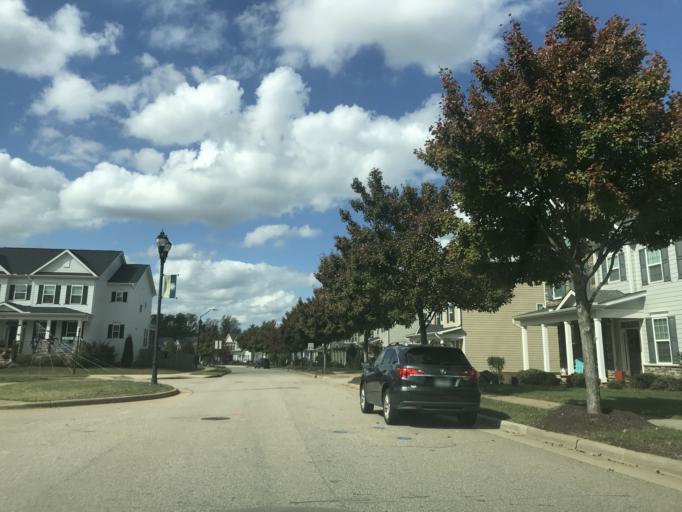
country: US
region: North Carolina
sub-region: Wake County
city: Raleigh
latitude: 35.7381
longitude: -78.6573
